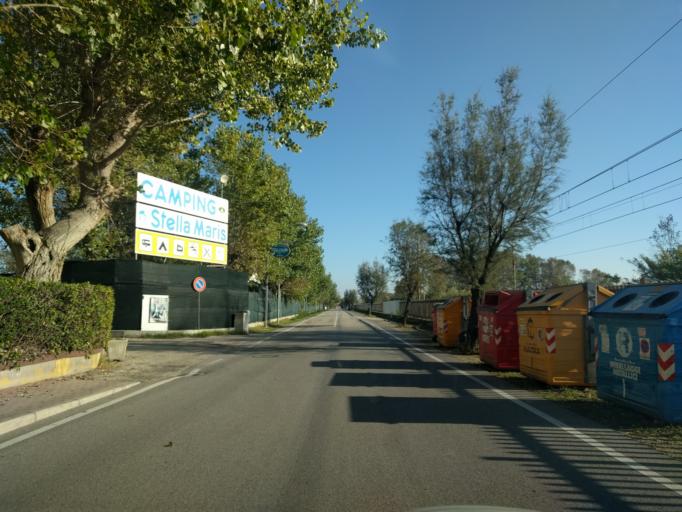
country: IT
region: The Marches
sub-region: Provincia di Pesaro e Urbino
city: Marotta
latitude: 43.7987
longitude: 13.0949
